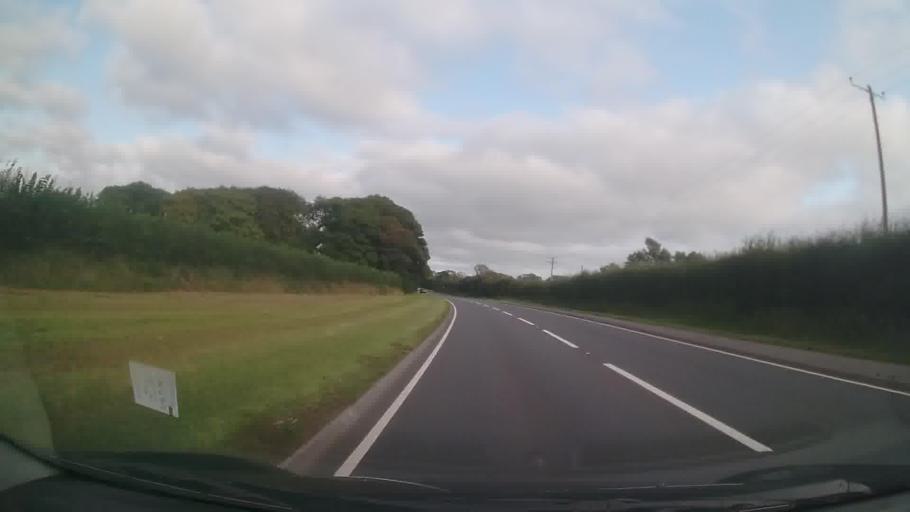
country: GB
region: Wales
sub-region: Pembrokeshire
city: Pembroke
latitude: 51.6896
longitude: -4.9091
